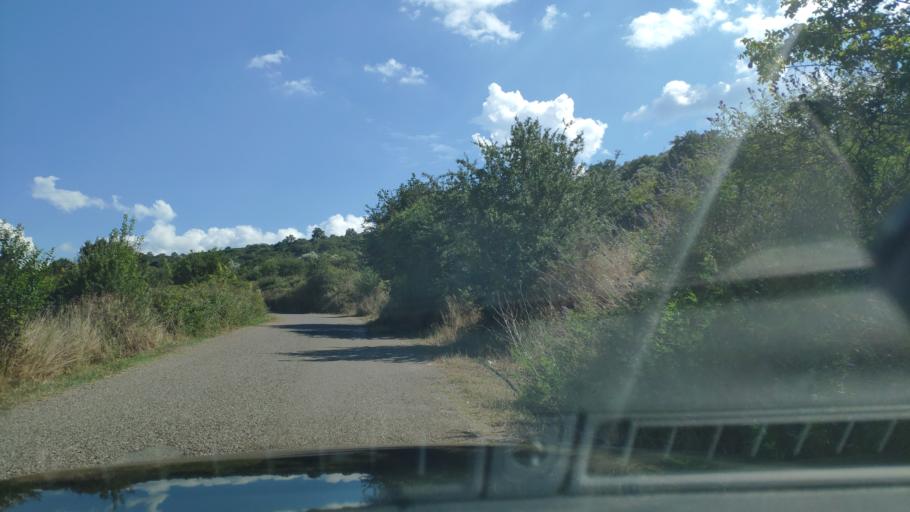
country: GR
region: West Greece
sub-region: Nomos Aitolias kai Akarnanias
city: Katouna
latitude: 38.8151
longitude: 21.1053
